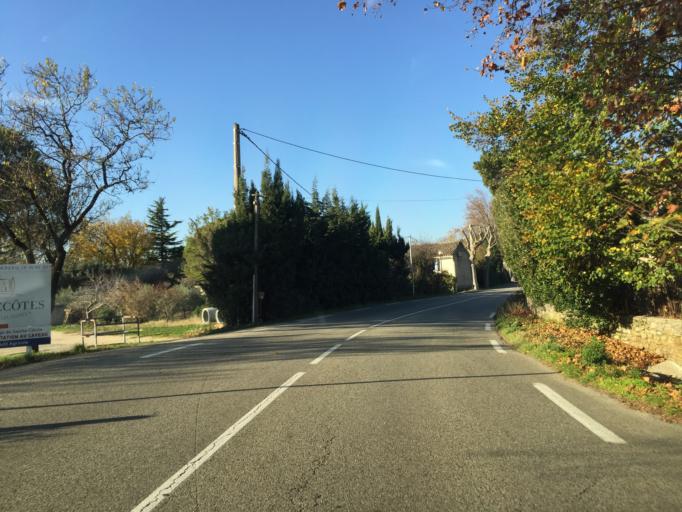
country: FR
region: Provence-Alpes-Cote d'Azur
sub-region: Departement du Vaucluse
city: Sainte-Cecile-les-Vignes
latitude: 44.2437
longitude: 4.8932
